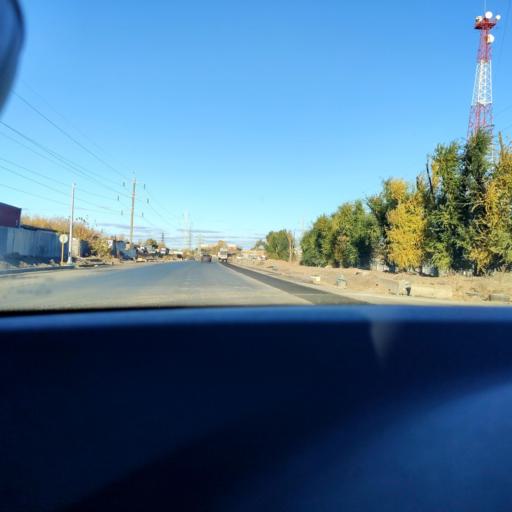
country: RU
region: Samara
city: Samara
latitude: 53.1915
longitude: 50.2278
